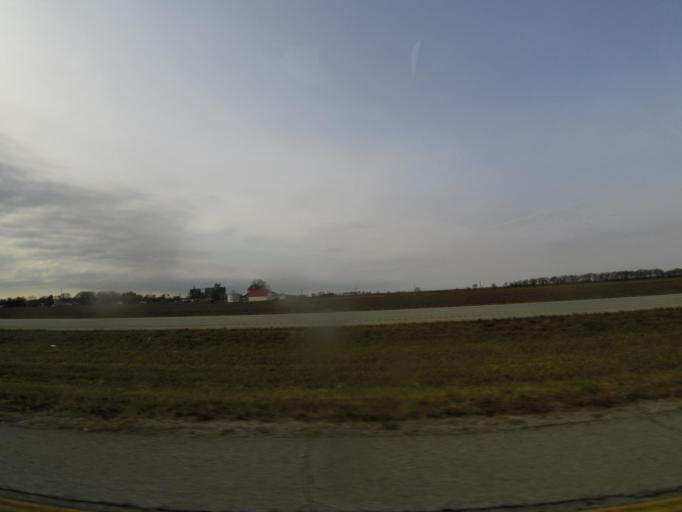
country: US
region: Illinois
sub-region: Christian County
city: Assumption
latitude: 39.5285
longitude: -89.0382
